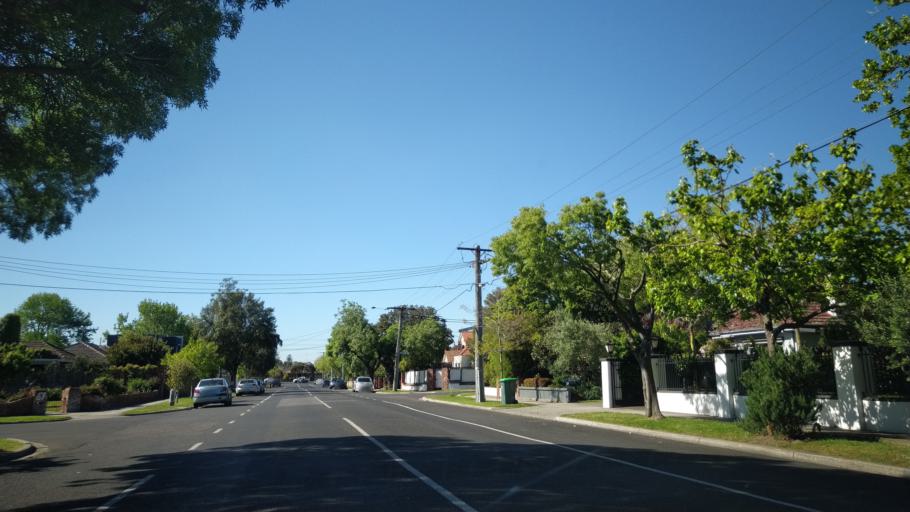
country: AU
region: Victoria
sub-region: Bayside
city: Brighton East
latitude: -37.9040
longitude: 145.0231
